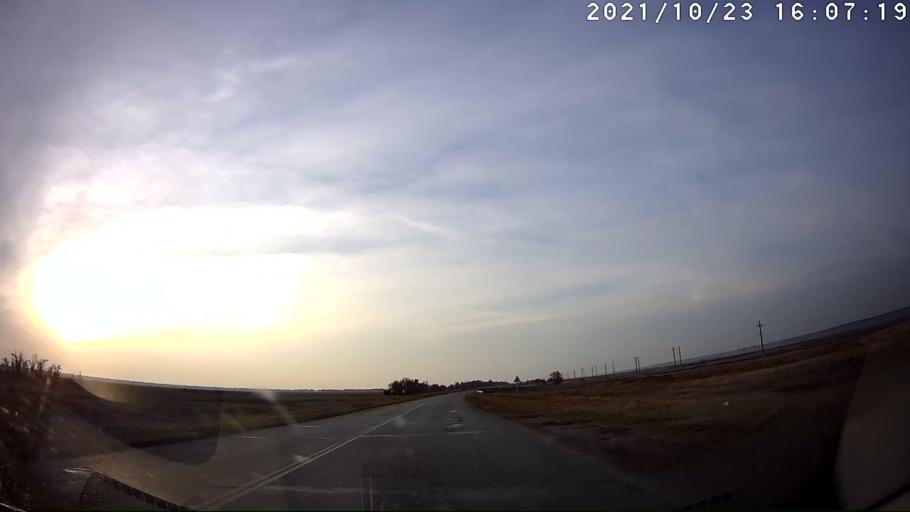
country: RU
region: Volgograd
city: Kotel'nikovo
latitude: 47.9332
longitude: 43.7385
